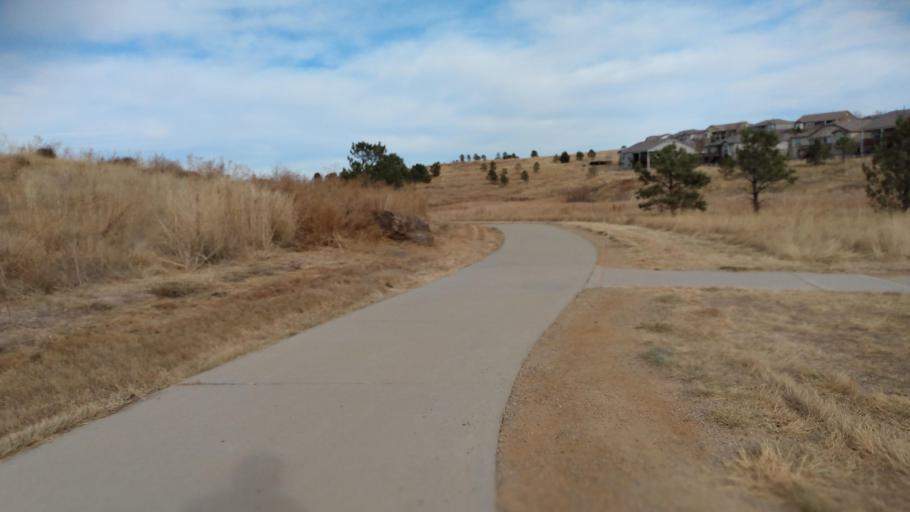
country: US
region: Colorado
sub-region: Boulder County
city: Lafayette
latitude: 39.9954
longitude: -105.0520
